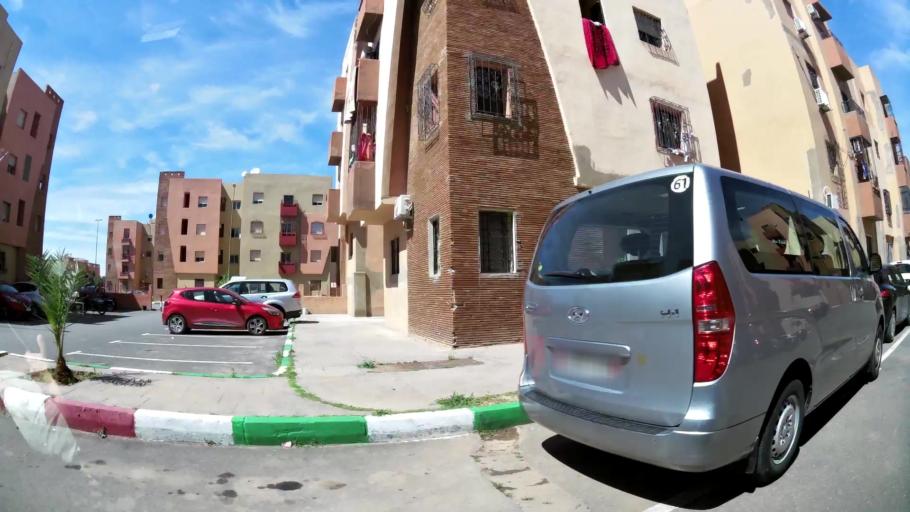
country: MA
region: Marrakech-Tensift-Al Haouz
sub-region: Marrakech
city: Marrakesh
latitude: 31.6357
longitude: -8.0796
